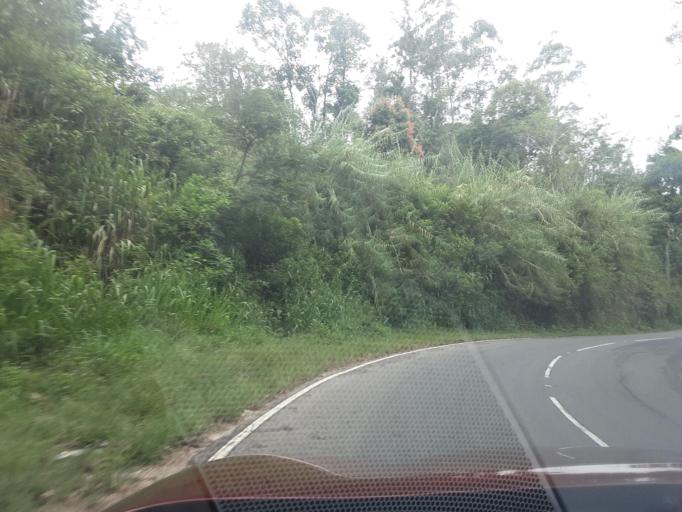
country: LK
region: Uva
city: Haputale
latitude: 6.8543
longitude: 80.9691
